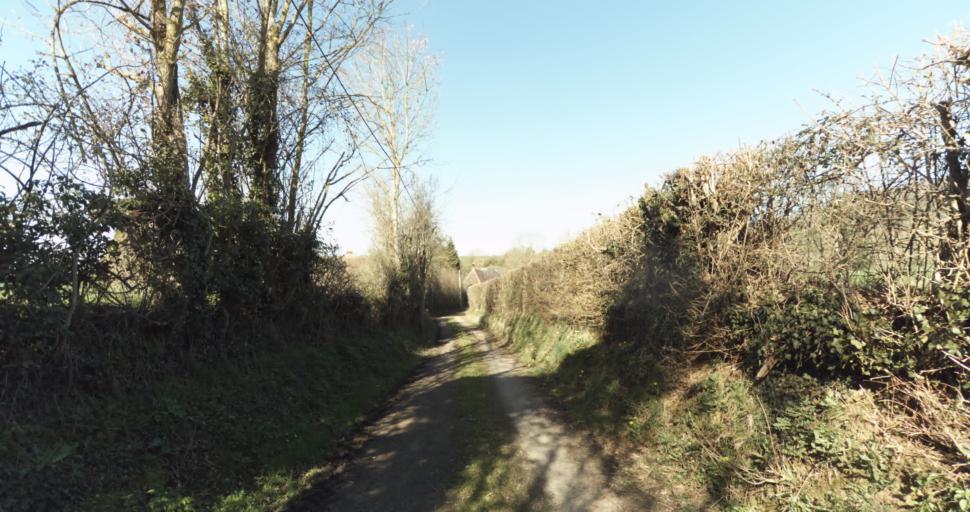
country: FR
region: Lower Normandy
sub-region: Departement du Calvados
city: Saint-Pierre-sur-Dives
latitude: 48.9734
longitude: 0.0523
